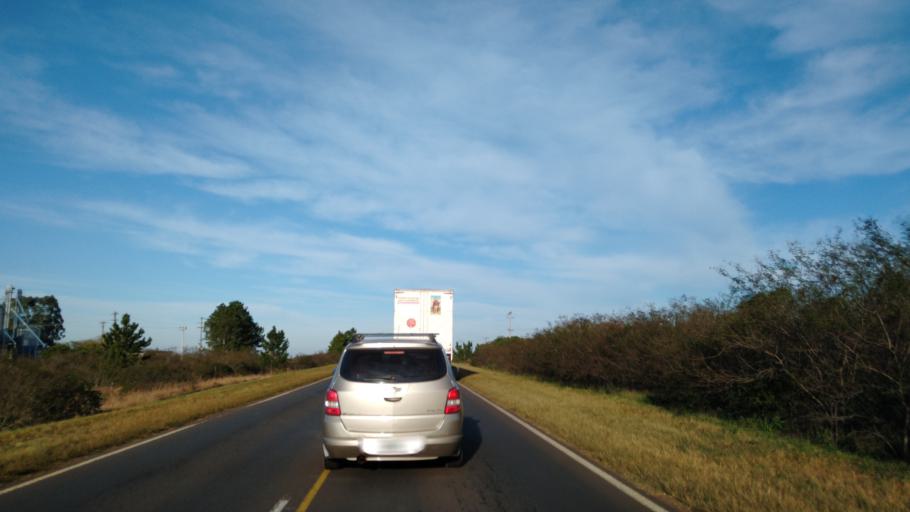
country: AR
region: Corrientes
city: La Cruz
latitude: -29.2081
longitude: -56.6989
